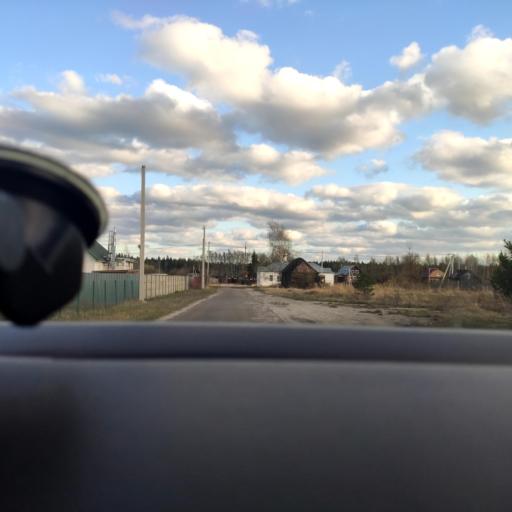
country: RU
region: Moskovskaya
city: Shaturtorf
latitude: 55.4352
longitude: 39.4271
